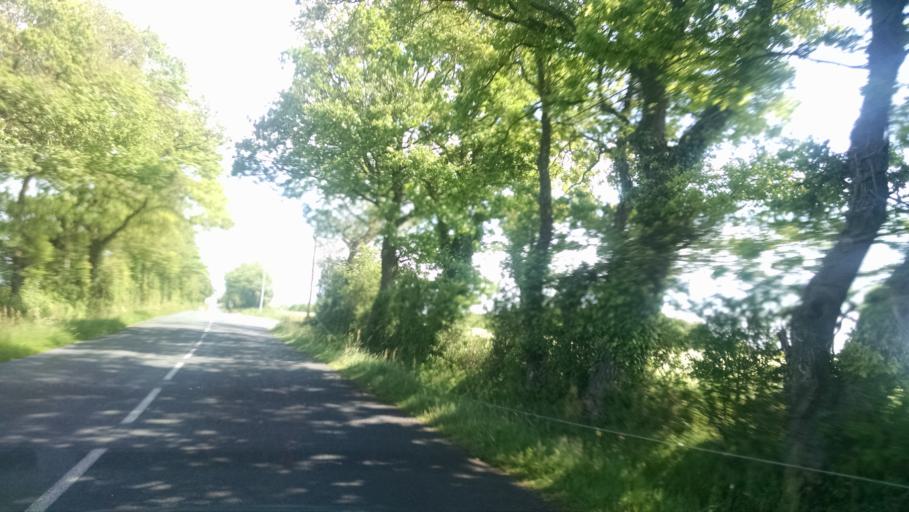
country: FR
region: Pays de la Loire
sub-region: Departement de la Vendee
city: Saint-Hilaire-de-Loulay
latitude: 47.0226
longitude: -1.3340
